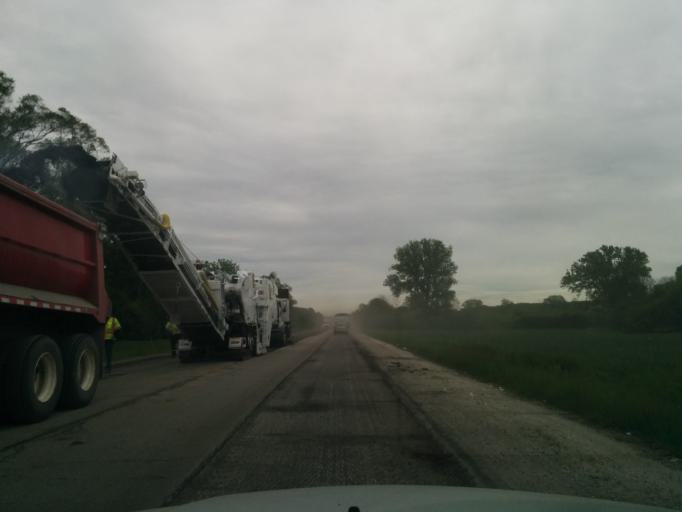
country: US
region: Illinois
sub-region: Cook County
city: Palos Park
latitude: 41.6851
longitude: -87.8707
